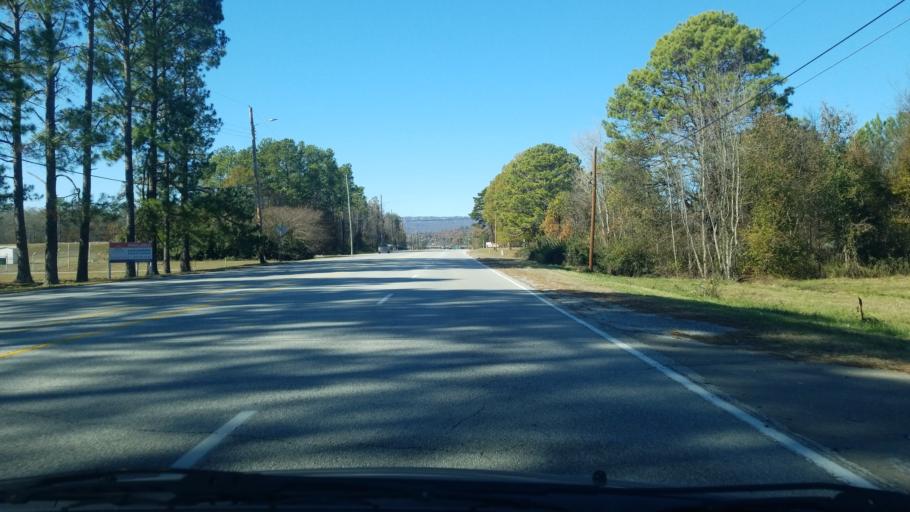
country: US
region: Tennessee
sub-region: Hamilton County
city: East Chattanooga
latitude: 35.1091
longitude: -85.2434
